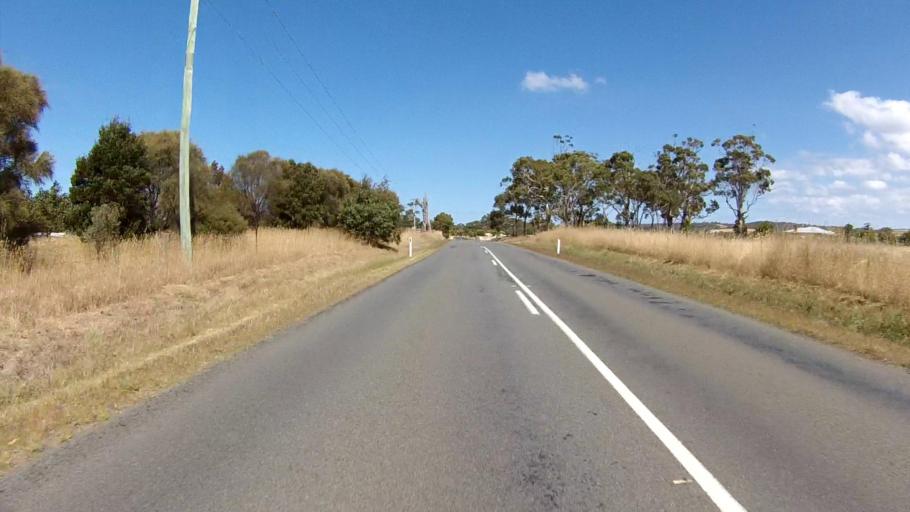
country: AU
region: Tasmania
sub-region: Break O'Day
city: St Helens
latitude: -42.1108
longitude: 148.0560
